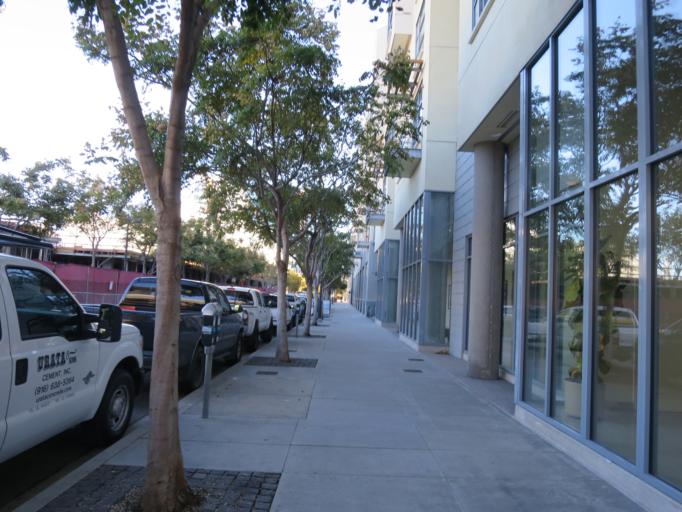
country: US
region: California
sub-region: San Francisco County
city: San Francisco
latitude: 37.7726
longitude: -122.3973
